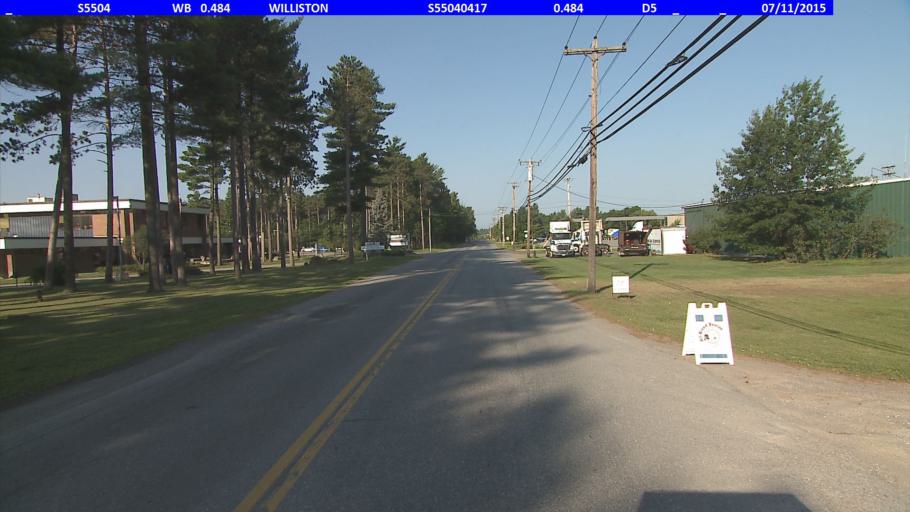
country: US
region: Vermont
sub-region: Chittenden County
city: Essex Junction
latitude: 44.4618
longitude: -73.1227
